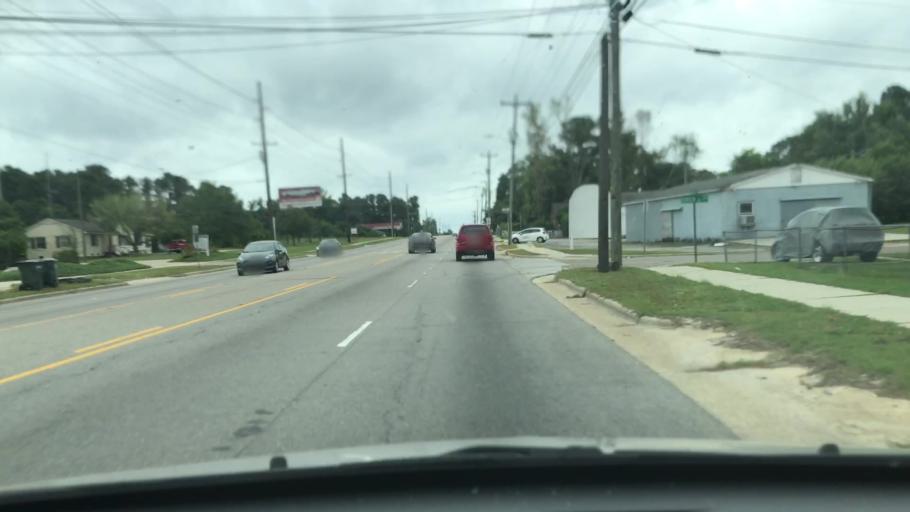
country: US
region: North Carolina
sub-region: Cumberland County
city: Fayetteville
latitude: 35.1059
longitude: -78.9232
